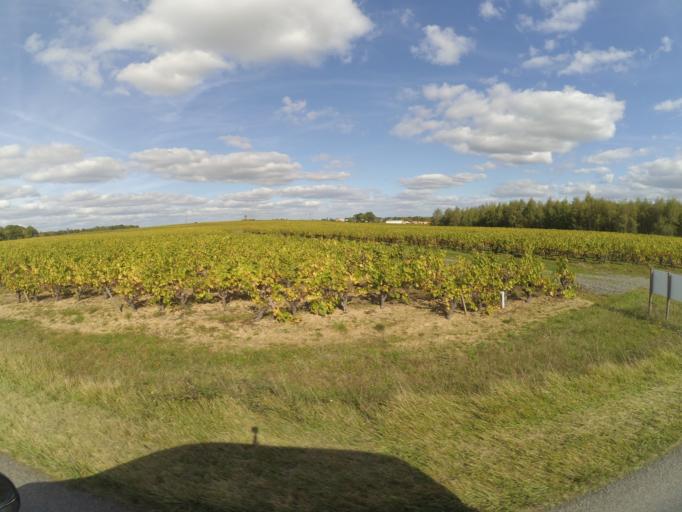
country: FR
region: Pays de la Loire
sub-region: Departement de la Loire-Atlantique
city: Monnieres
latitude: 47.1158
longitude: -1.3558
